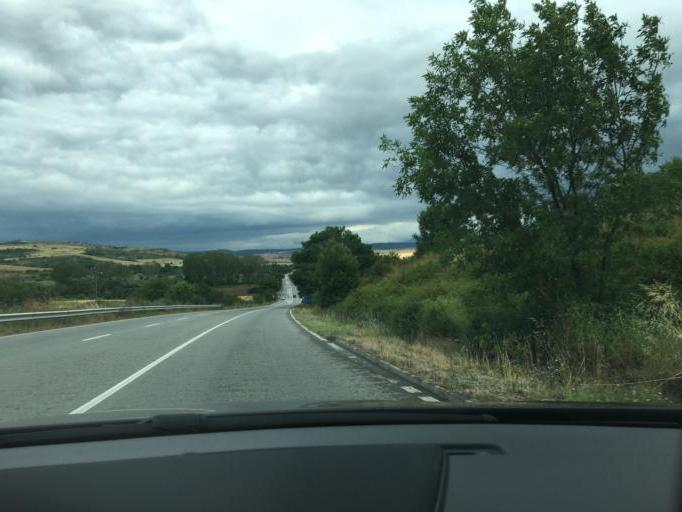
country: BG
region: Kyustendil
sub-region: Obshtina Dupnitsa
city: Dupnitsa
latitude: 42.2675
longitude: 23.0614
